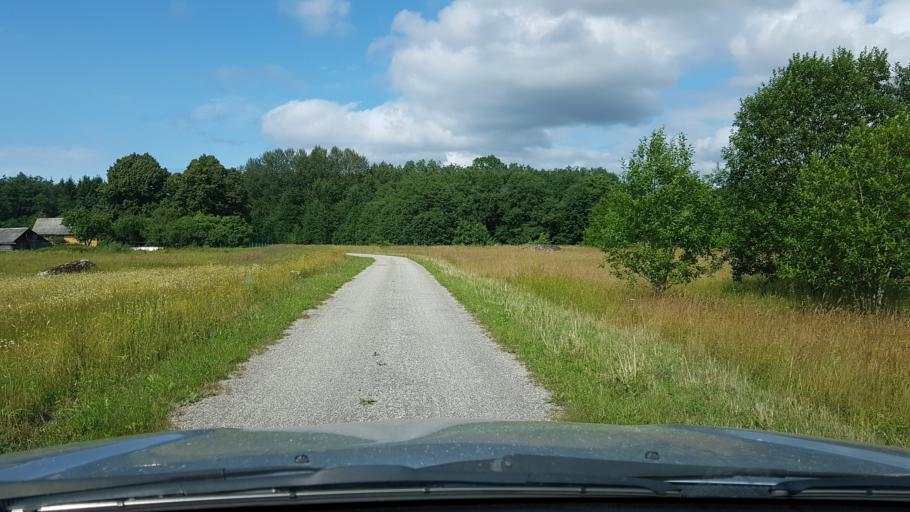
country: EE
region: Ida-Virumaa
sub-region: Narva-Joesuu linn
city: Narva-Joesuu
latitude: 59.3753
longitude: 27.9573
